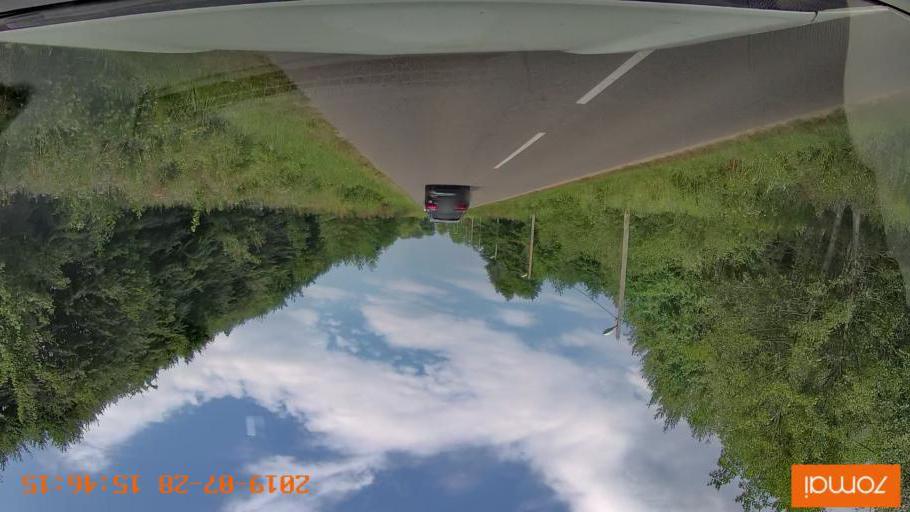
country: RU
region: Kaliningrad
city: Otradnoye
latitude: 54.9425
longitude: 20.0513
